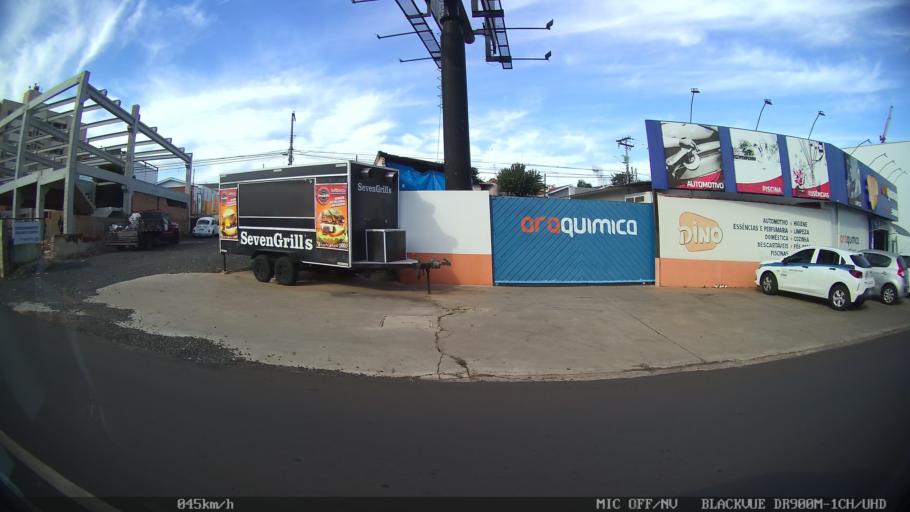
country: BR
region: Sao Paulo
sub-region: Araraquara
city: Araraquara
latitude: -21.7990
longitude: -48.1729
